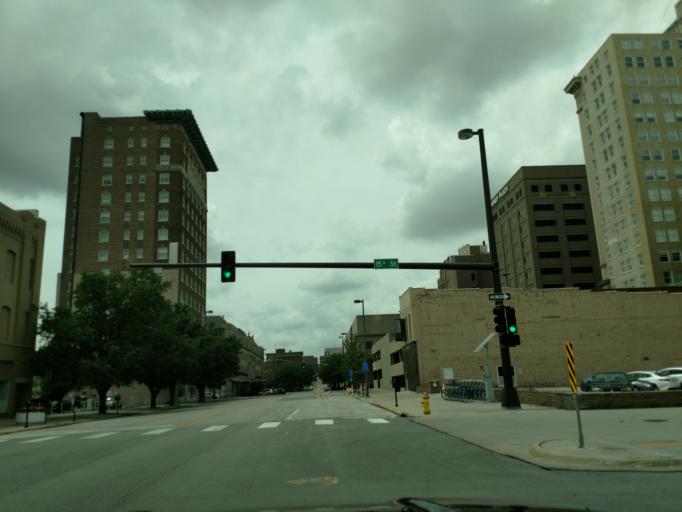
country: US
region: Nebraska
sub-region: Douglas County
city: Omaha
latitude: 41.2555
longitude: -95.9358
